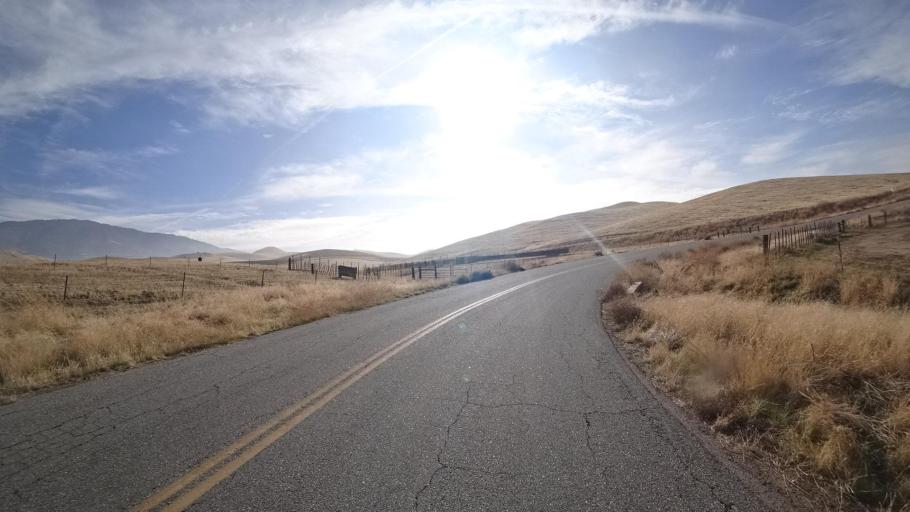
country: US
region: California
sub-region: Kern County
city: Bear Valley Springs
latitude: 35.2763
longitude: -118.6884
